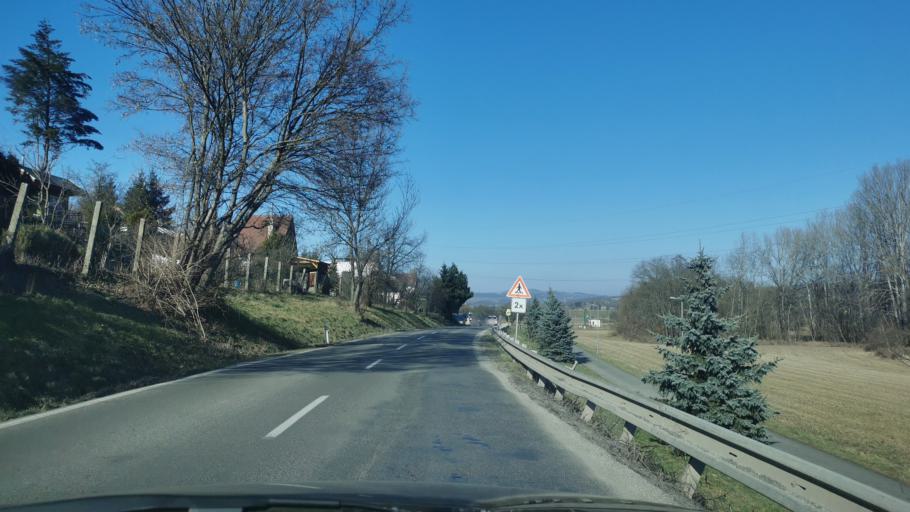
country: SK
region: Trnavsky
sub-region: Okres Senica
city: Senica
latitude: 48.6952
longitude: 17.3988
